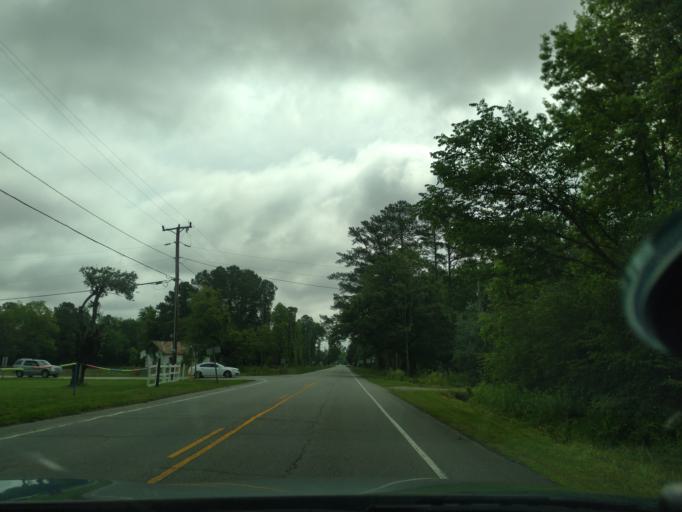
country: US
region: North Carolina
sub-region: Washington County
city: Plymouth
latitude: 35.8756
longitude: -76.6654
